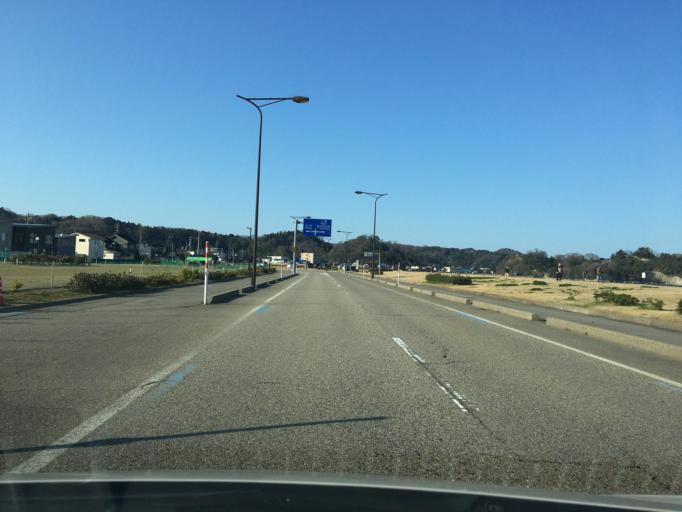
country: JP
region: Toyama
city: Himi
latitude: 36.8723
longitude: 136.9845
